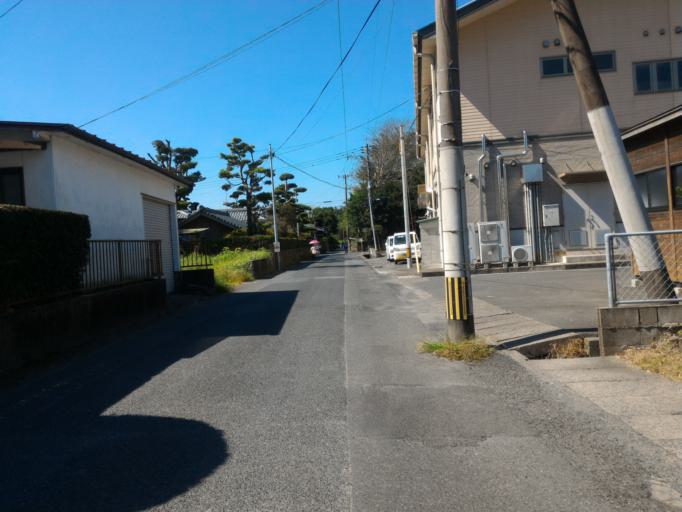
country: JP
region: Kagoshima
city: Kanoya
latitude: 31.3439
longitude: 130.9454
